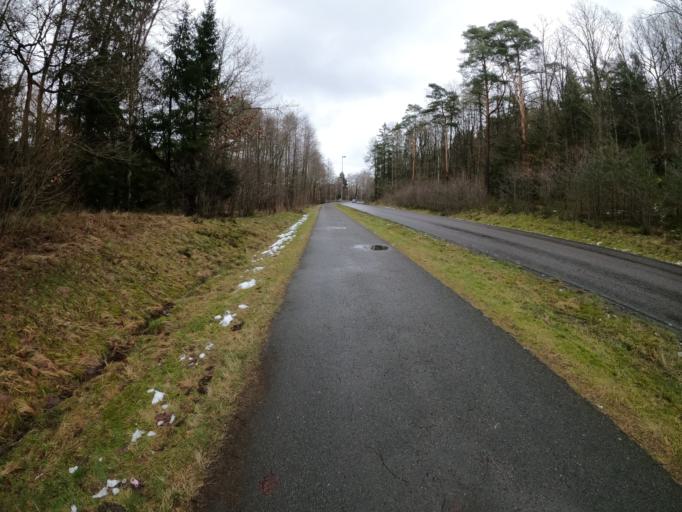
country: SE
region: Vaestra Goetaland
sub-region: Harryda Kommun
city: Molnlycke
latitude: 57.6433
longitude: 12.1139
